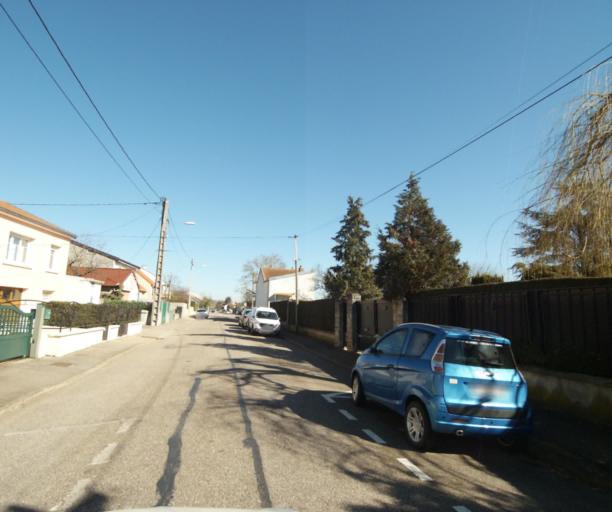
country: FR
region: Lorraine
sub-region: Departement de Meurthe-et-Moselle
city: Essey-les-Nancy
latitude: 48.7083
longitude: 6.2347
